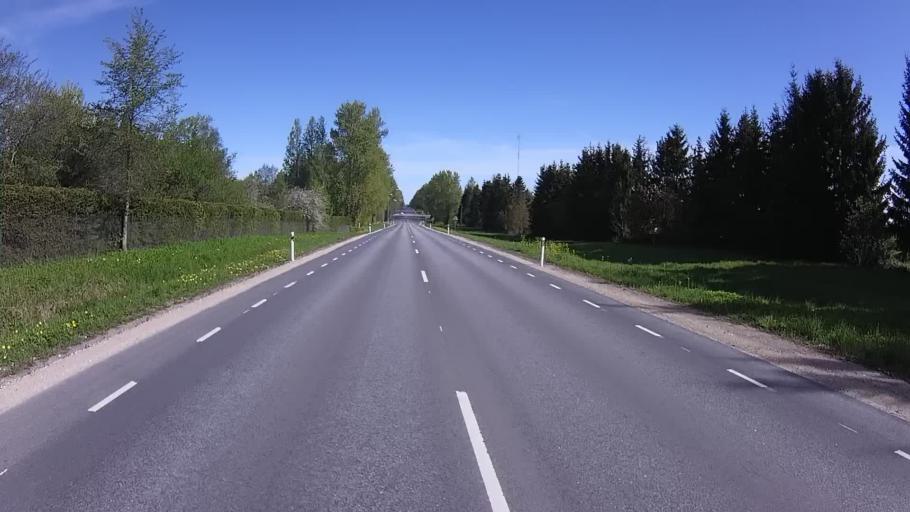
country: EE
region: Polvamaa
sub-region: Polva linn
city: Polva
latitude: 58.2784
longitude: 27.0024
